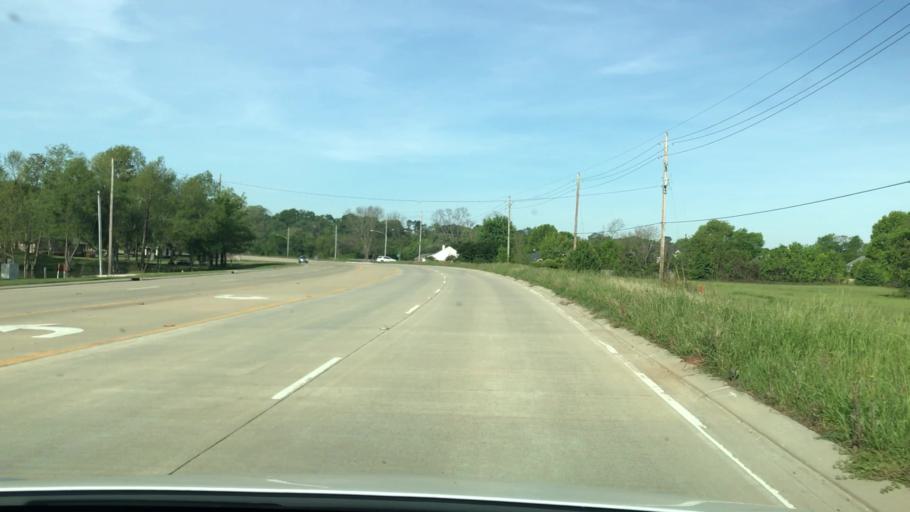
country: US
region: Louisiana
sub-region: Bossier Parish
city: Bossier City
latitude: 32.4000
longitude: -93.7183
